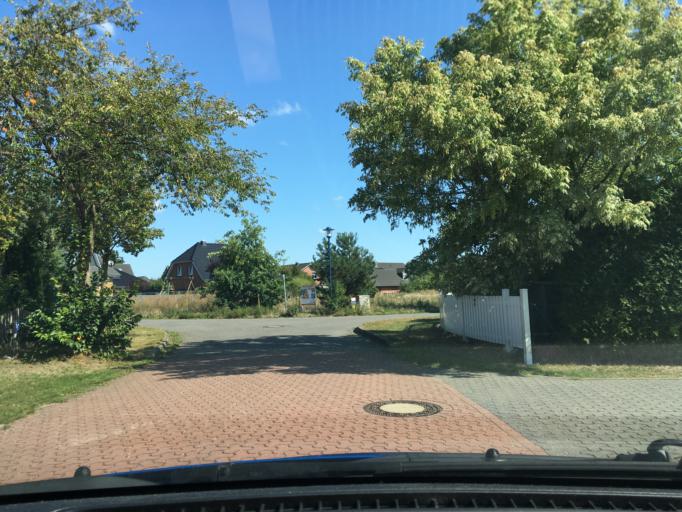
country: DE
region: Lower Saxony
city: Winsen
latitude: 52.6916
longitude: 9.9174
